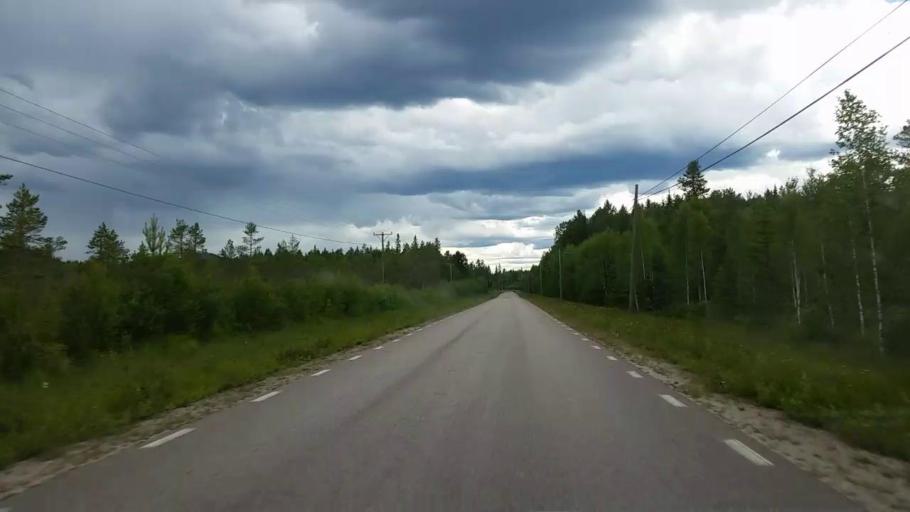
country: SE
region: Gaevleborg
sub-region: Ovanakers Kommun
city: Edsbyn
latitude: 61.4531
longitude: 15.8785
